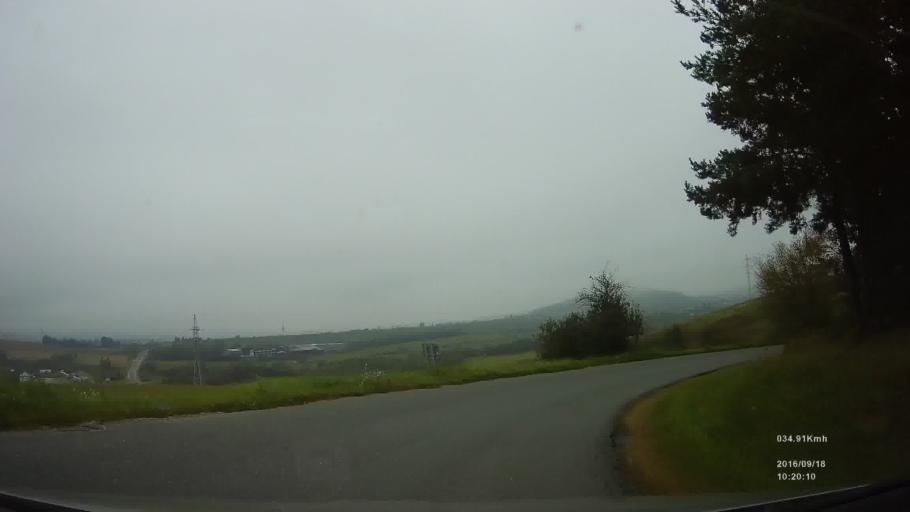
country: SK
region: Kosicky
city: Spisska Nova Ves
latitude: 48.9395
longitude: 20.6065
